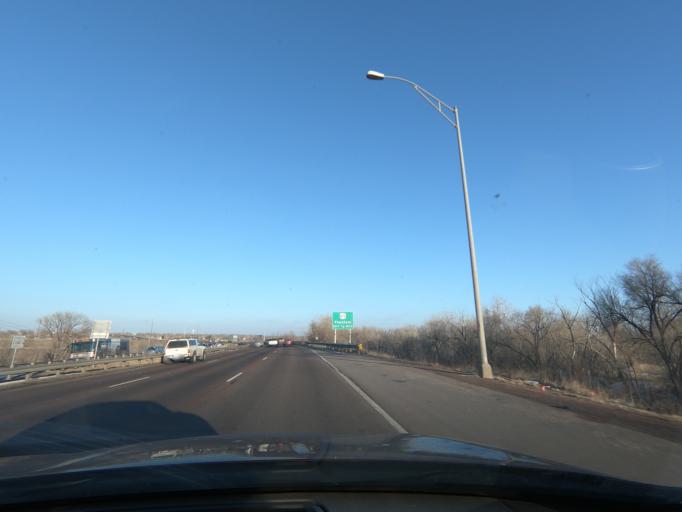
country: US
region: Colorado
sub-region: El Paso County
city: Stratmoor
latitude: 38.7647
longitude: -104.7685
